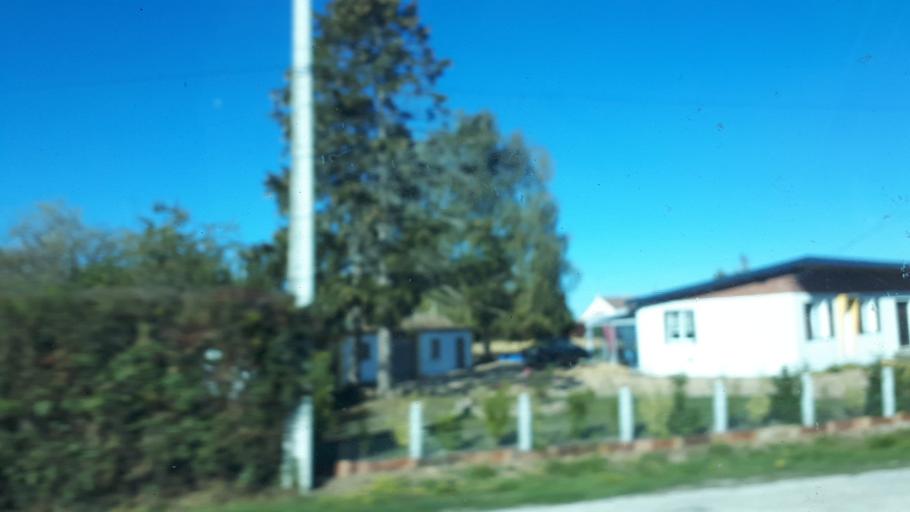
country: FR
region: Centre
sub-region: Departement du Loir-et-Cher
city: Moree
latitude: 47.9215
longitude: 1.1927
